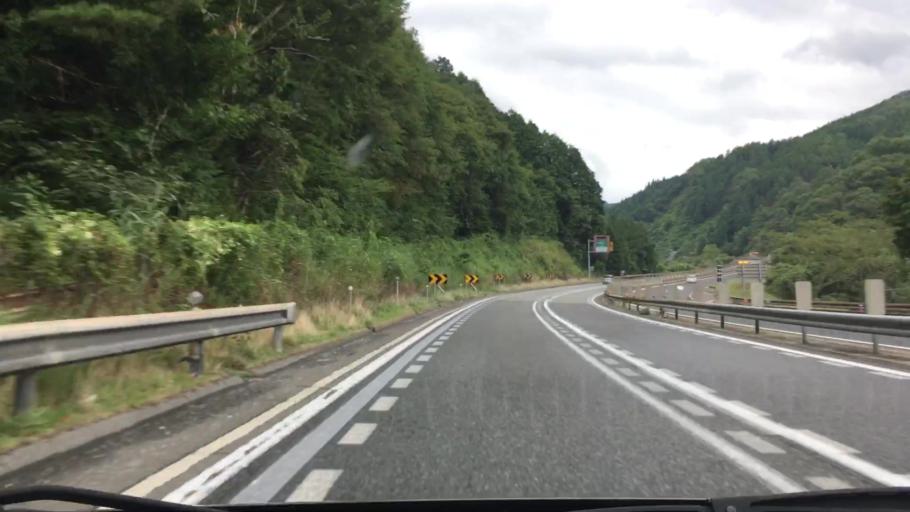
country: JP
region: Okayama
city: Niimi
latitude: 35.0269
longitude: 133.5253
